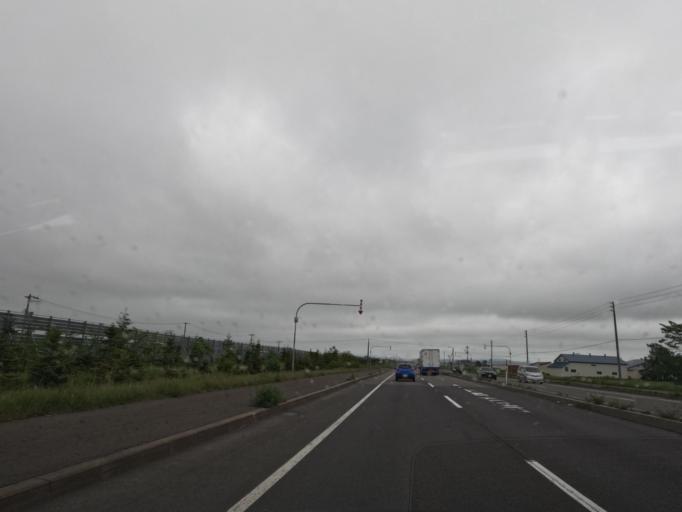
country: JP
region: Hokkaido
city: Tobetsu
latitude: 43.1665
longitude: 141.5203
